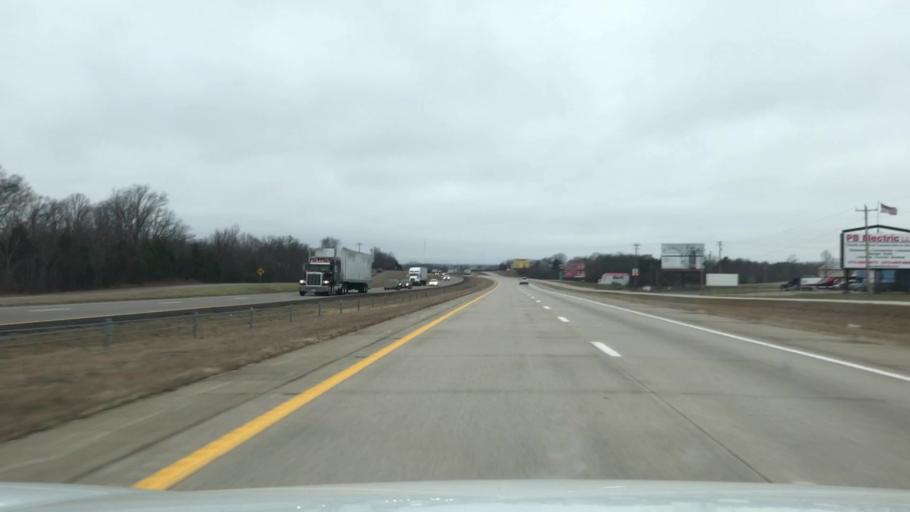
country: US
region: Missouri
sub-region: Crawford County
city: Bourbon
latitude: 38.1800
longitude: -91.2060
